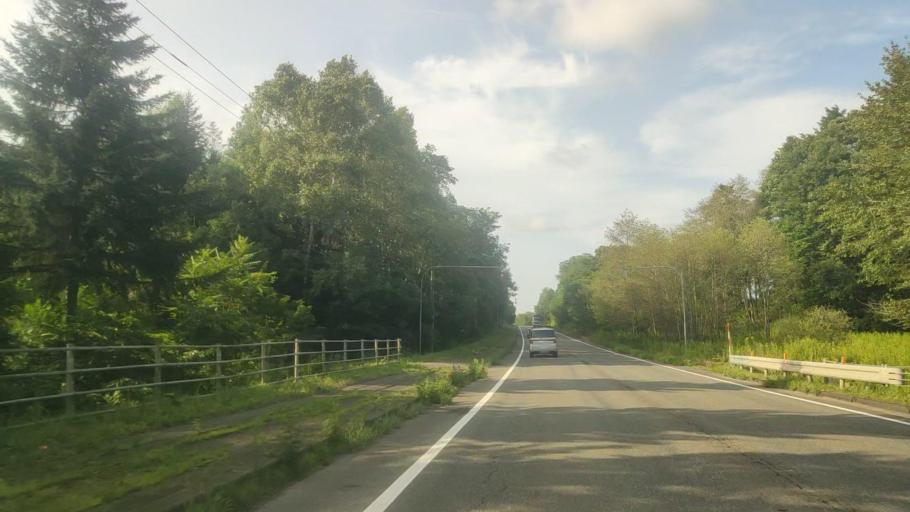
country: JP
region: Hokkaido
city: Chitose
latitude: 42.8683
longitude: 141.8226
